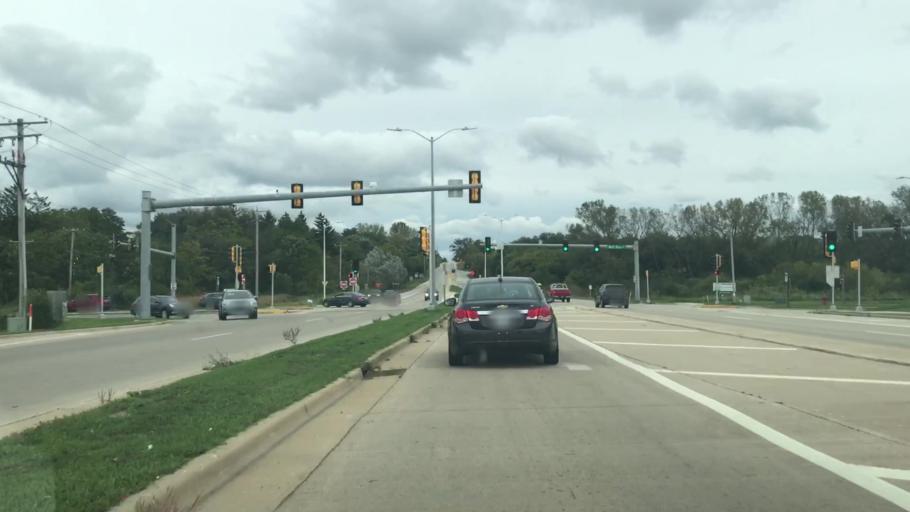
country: US
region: Wisconsin
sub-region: Waukesha County
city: Mukwonago
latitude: 42.8491
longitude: -88.3190
